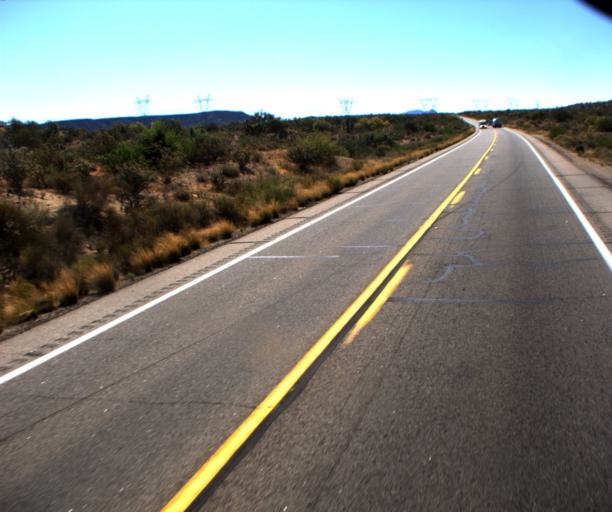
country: US
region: Arizona
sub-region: Yavapai County
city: Bagdad
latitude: 34.3472
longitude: -113.1612
